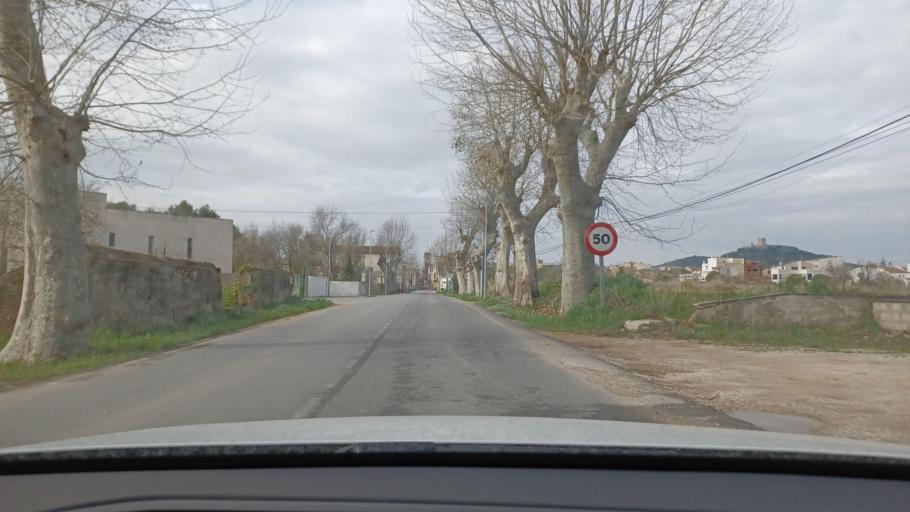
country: ES
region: Catalonia
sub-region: Provincia de Tarragona
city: Ulldecona
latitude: 40.6011
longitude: 0.4519
